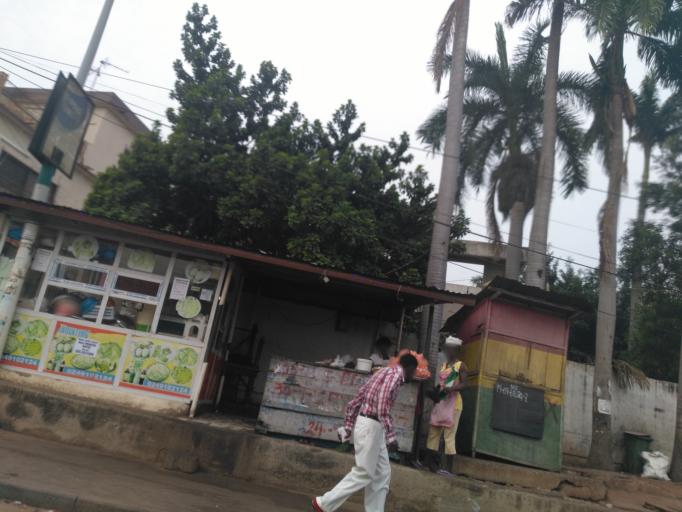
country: GH
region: Greater Accra
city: Dome
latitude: 5.5998
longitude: -0.2242
